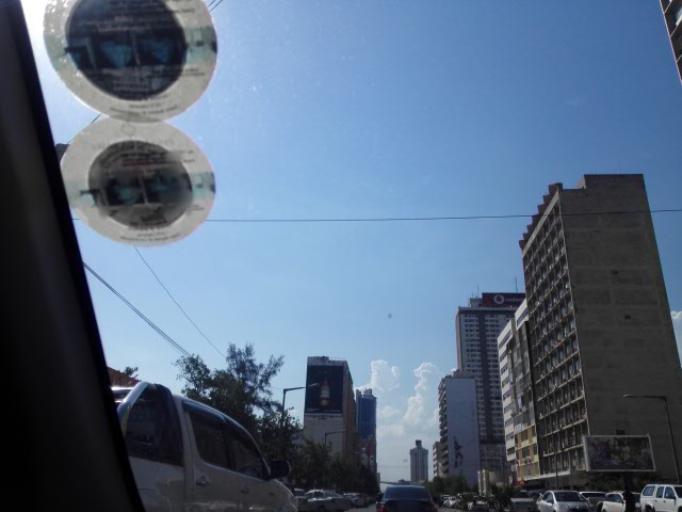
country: MZ
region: Maputo City
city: Maputo
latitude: -25.9761
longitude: 32.5768
